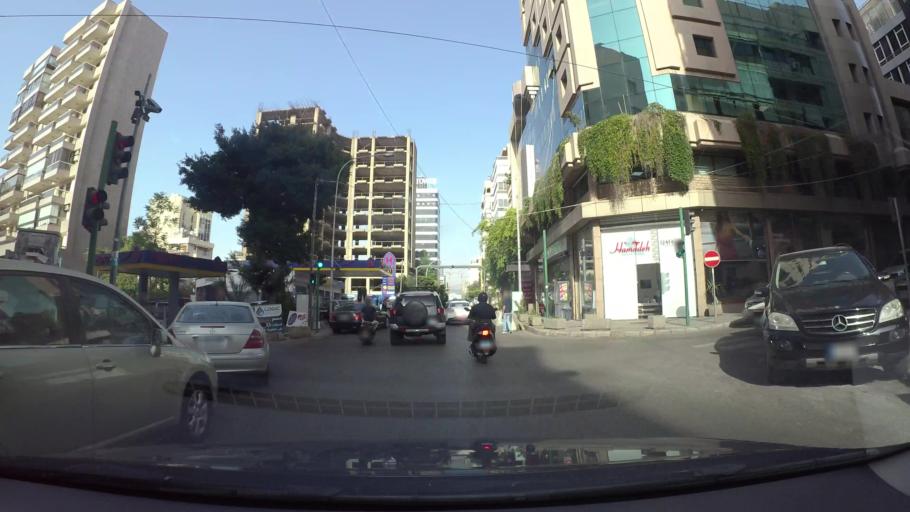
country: LB
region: Beyrouth
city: Ra's Bayrut
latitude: 33.8941
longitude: 35.4852
